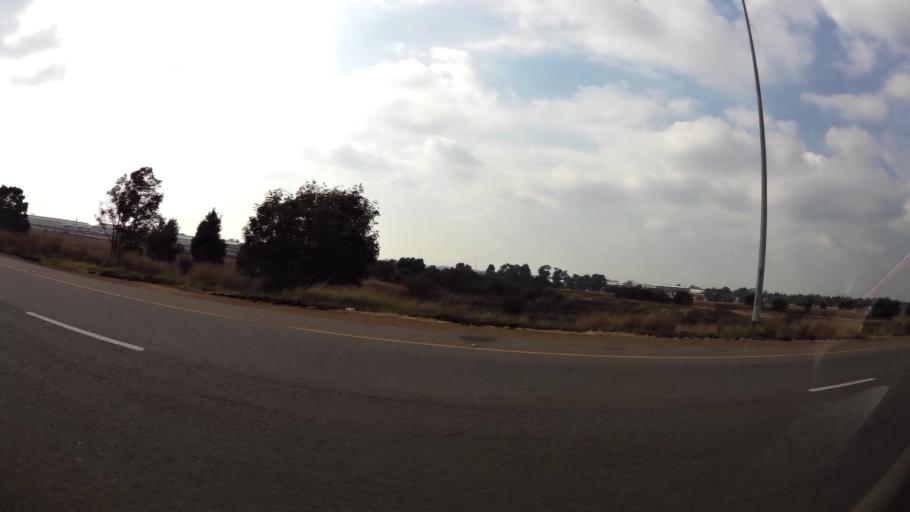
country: ZA
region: Gauteng
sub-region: City of Johannesburg Metropolitan Municipality
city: Modderfontein
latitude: -26.1079
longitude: 28.2548
